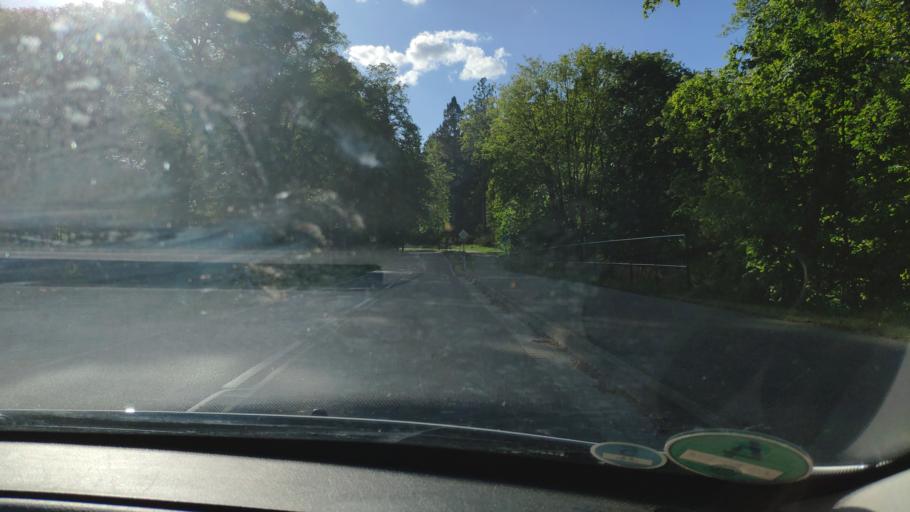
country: DE
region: Mecklenburg-Vorpommern
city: Neustrelitz
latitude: 53.3465
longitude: 13.0156
